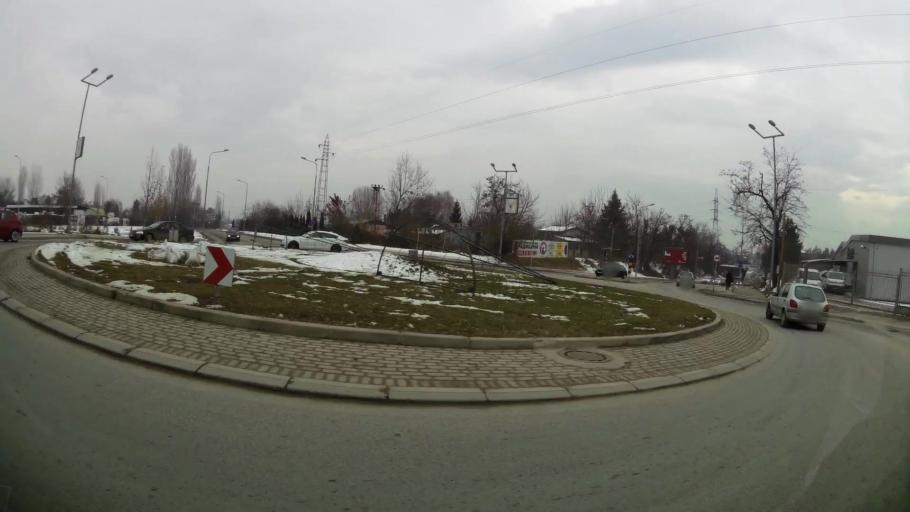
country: MK
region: Butel
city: Butel
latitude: 42.0278
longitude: 21.4444
